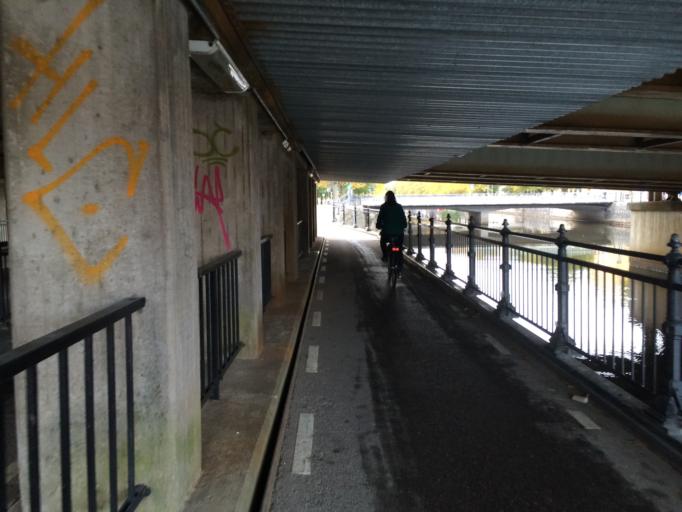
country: SE
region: Gaevleborg
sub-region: Gavle Kommun
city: Gavle
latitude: 60.6749
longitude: 17.1528
